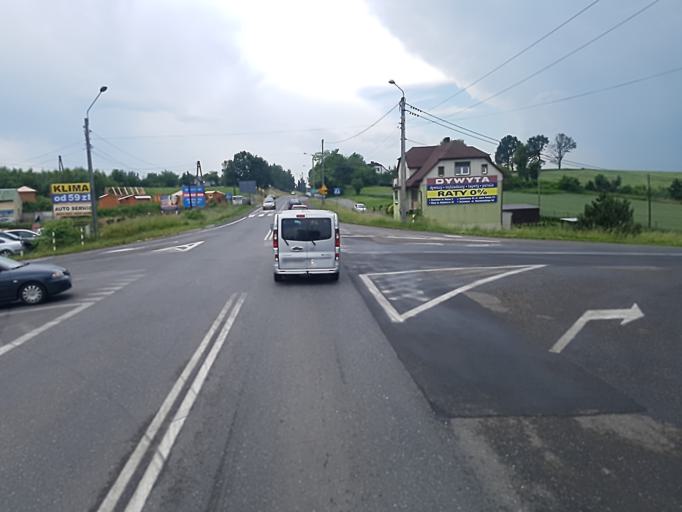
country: PL
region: Silesian Voivodeship
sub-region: Powiat wodzislawski
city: Mszana
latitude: 49.9666
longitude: 18.5464
